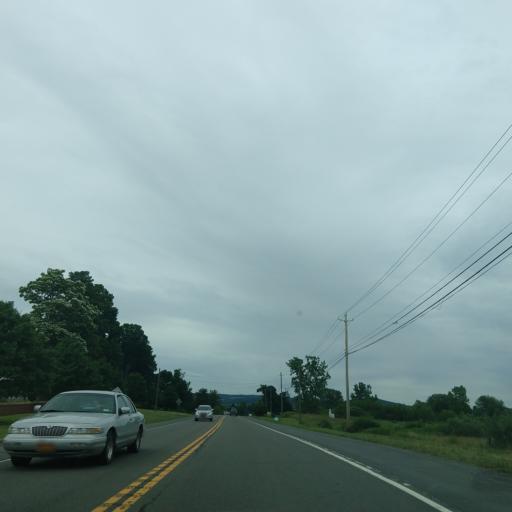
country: US
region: New York
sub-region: Tompkins County
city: Dryden
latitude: 42.4875
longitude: -76.3386
